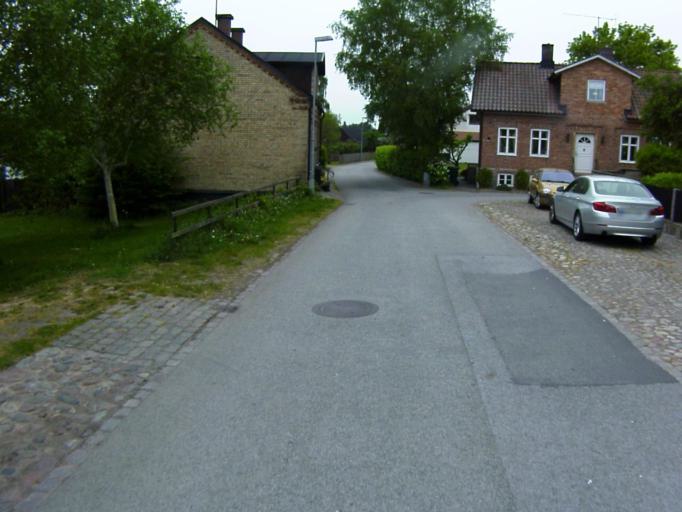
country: SE
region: Skane
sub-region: Kristianstads Kommun
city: Ahus
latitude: 55.9209
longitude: 14.2913
